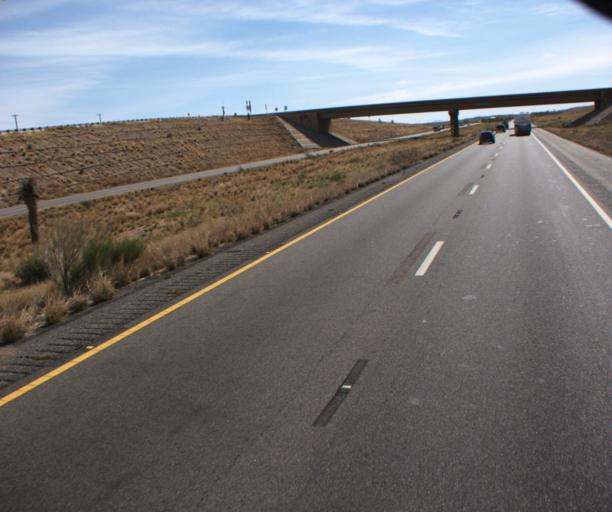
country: US
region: Arizona
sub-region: Cochise County
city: Mescal
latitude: 31.9819
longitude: -110.5382
